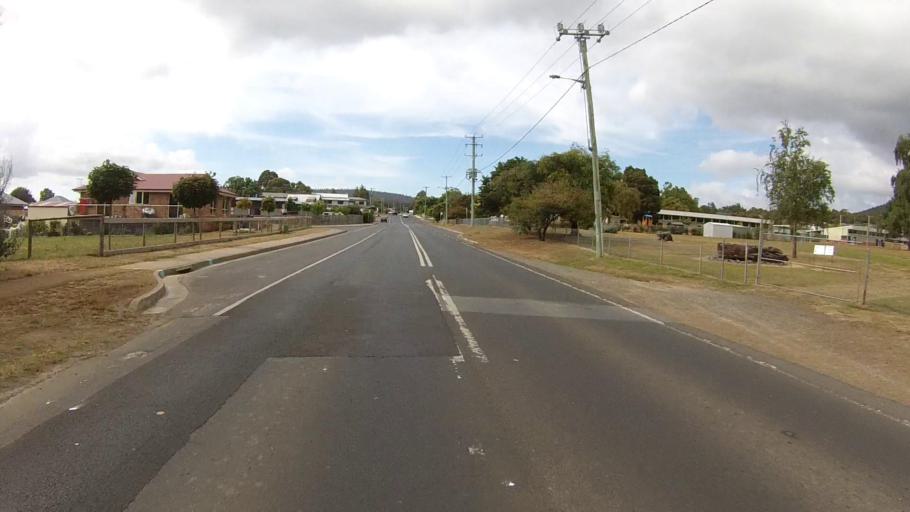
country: AU
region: Tasmania
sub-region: Kingborough
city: Margate
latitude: -43.0642
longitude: 147.2540
